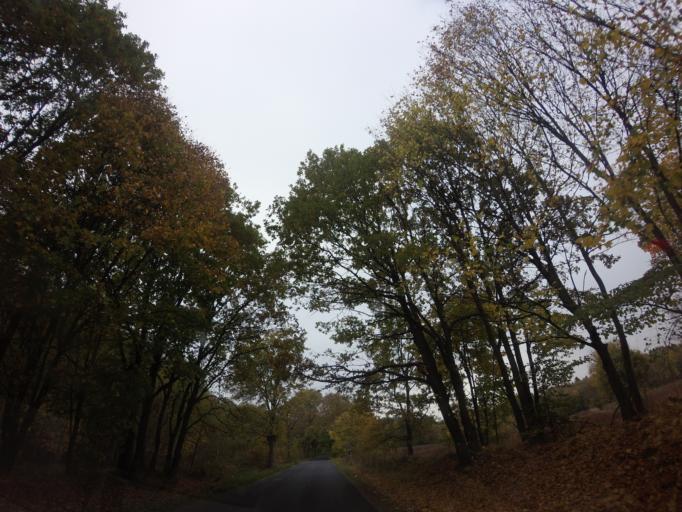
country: PL
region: West Pomeranian Voivodeship
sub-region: Powiat choszczenski
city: Recz
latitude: 53.1933
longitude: 15.6357
